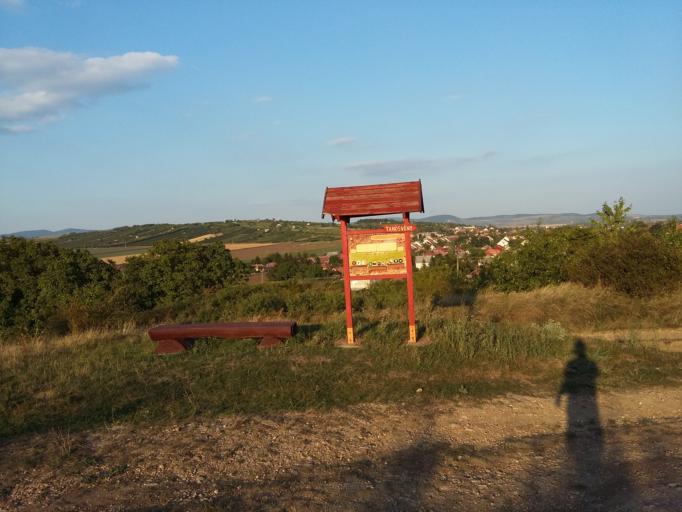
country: HU
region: Borsod-Abauj-Zemplen
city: Bekecs
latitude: 48.1611
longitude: 21.1758
